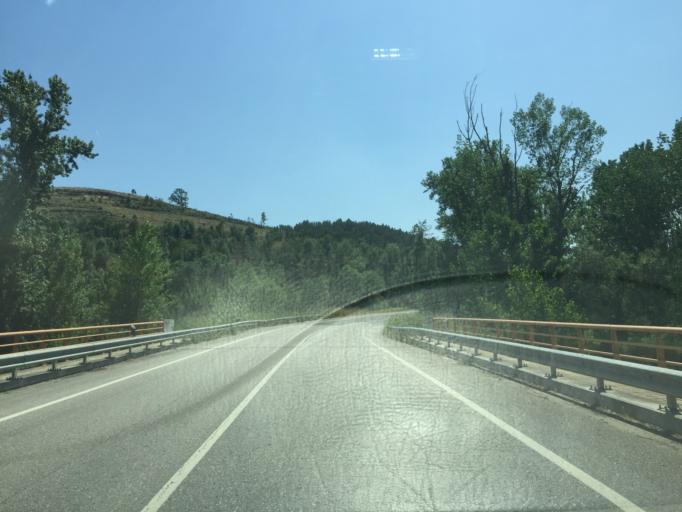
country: PT
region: Santarem
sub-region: Constancia
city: Constancia
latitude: 39.4612
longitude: -8.3450
